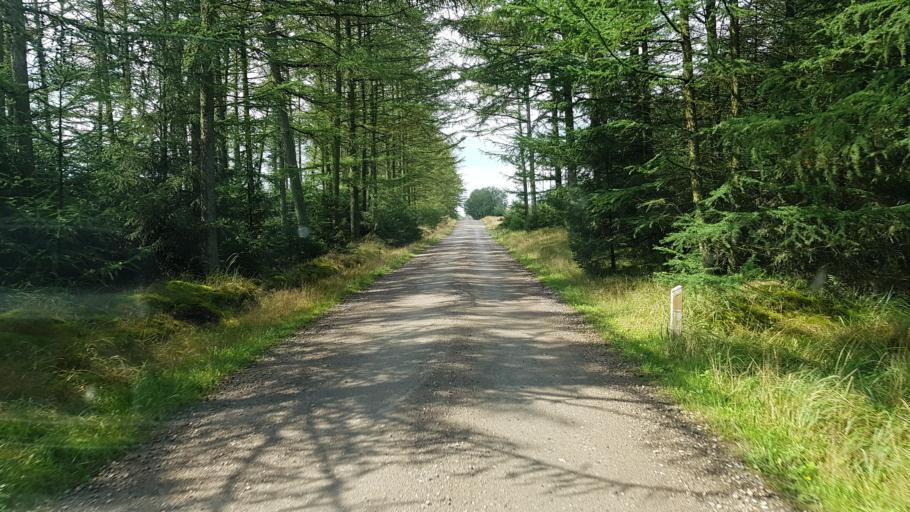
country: DK
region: South Denmark
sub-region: Vejen Kommune
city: Holsted
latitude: 55.5956
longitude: 8.8884
